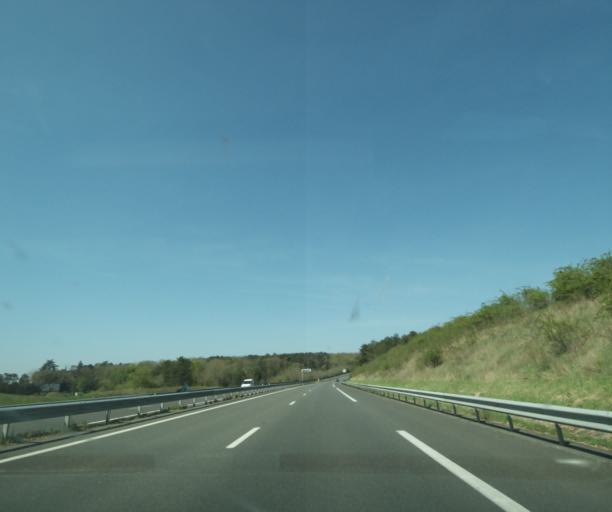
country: FR
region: Bourgogne
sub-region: Departement de la Nievre
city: Pouilly-sur-Loire
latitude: 47.2886
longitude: 2.9606
